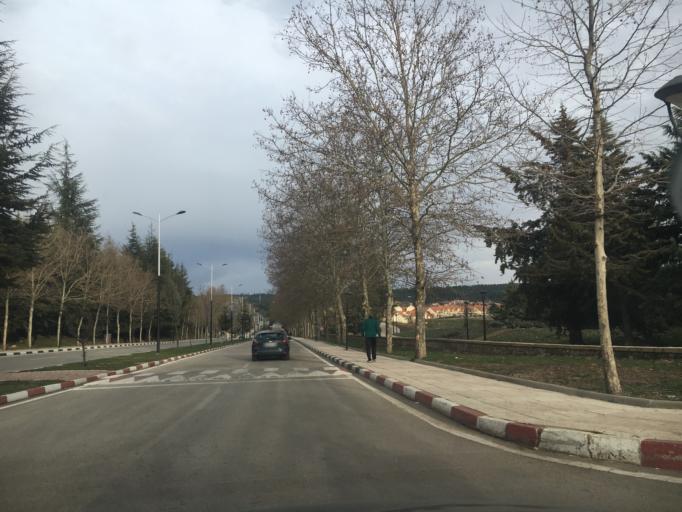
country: MA
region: Meknes-Tafilalet
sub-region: Ifrane
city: Ifrane
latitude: 33.5278
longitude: -5.1239
